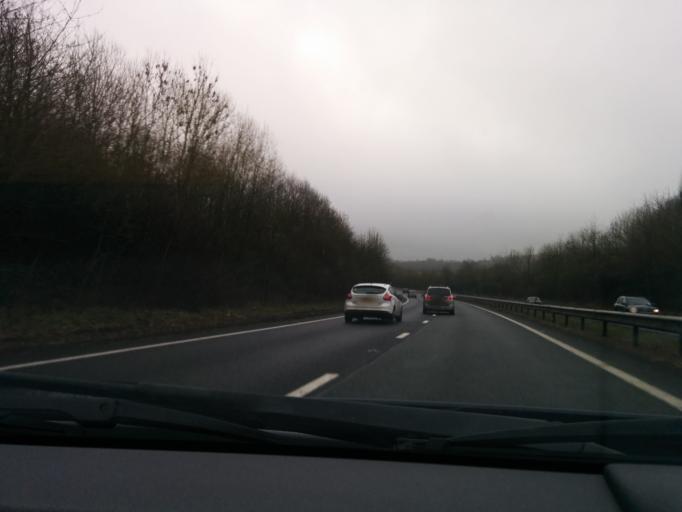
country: GB
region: England
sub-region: Hampshire
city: Highclere
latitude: 51.3268
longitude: -1.3459
